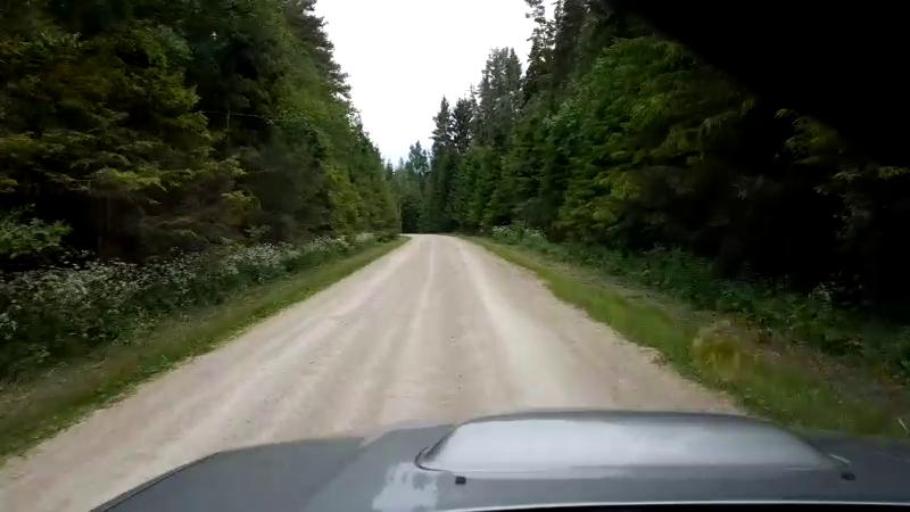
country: EE
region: Paernumaa
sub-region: Halinga vald
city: Parnu-Jaagupi
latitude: 58.5148
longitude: 24.5979
